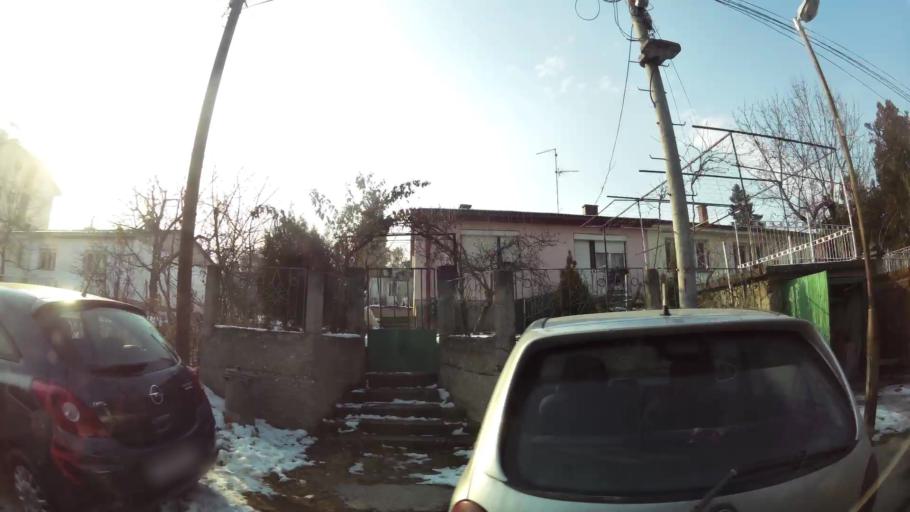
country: MK
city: Creshevo
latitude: 42.0146
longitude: 21.5085
